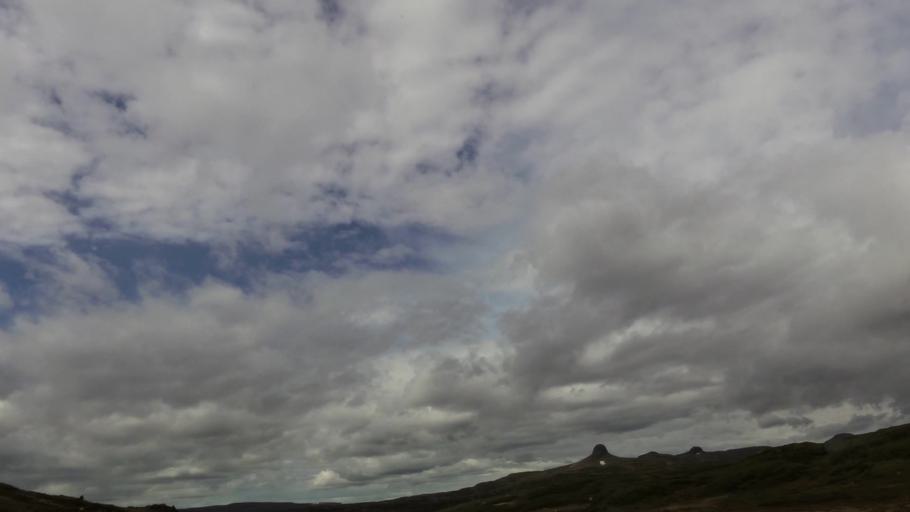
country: IS
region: West
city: Stykkisholmur
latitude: 65.5393
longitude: -22.0967
